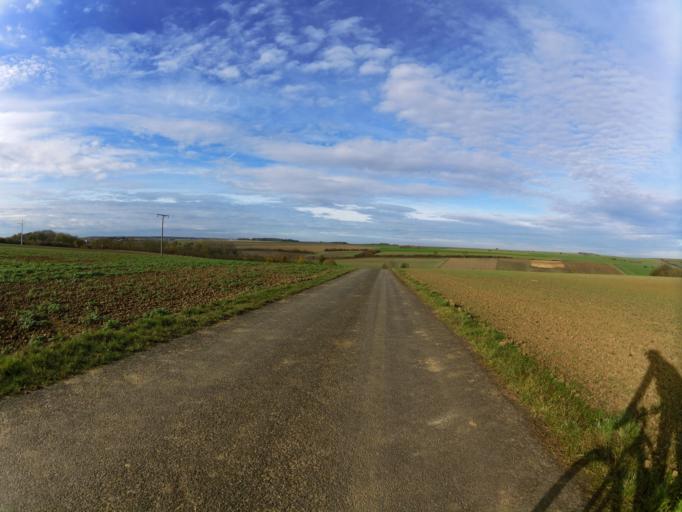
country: DE
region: Bavaria
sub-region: Regierungsbezirk Unterfranken
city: Giebelstadt
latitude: 49.6686
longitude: 9.9798
